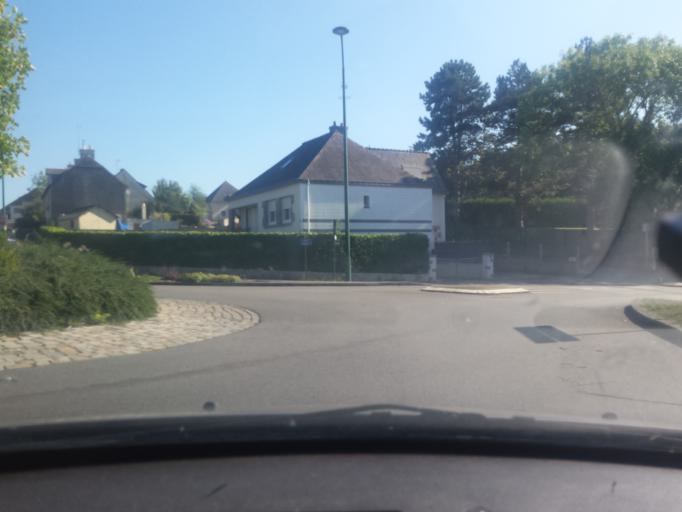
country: FR
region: Brittany
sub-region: Departement du Morbihan
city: Pontivy
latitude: 48.0623
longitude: -2.9586
